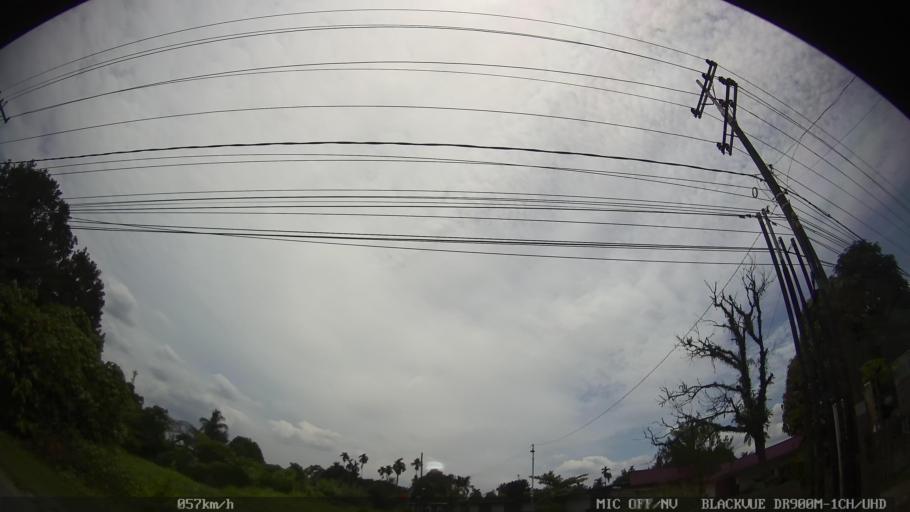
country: ID
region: North Sumatra
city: Sunggal
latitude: 3.5315
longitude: 98.6203
